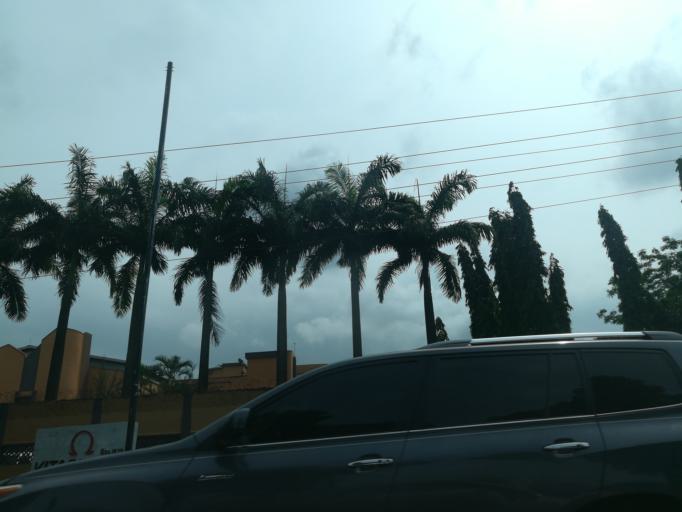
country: NG
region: Lagos
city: Ojota
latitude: 6.6060
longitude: 3.3706
